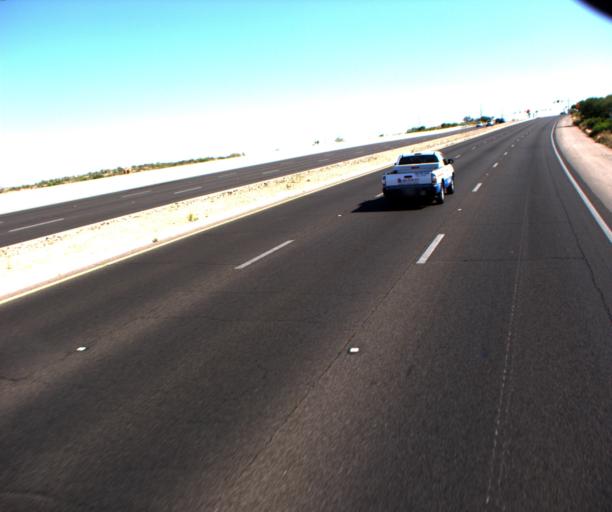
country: US
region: Arizona
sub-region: Pima County
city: Oro Valley
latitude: 32.4226
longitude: -110.9364
